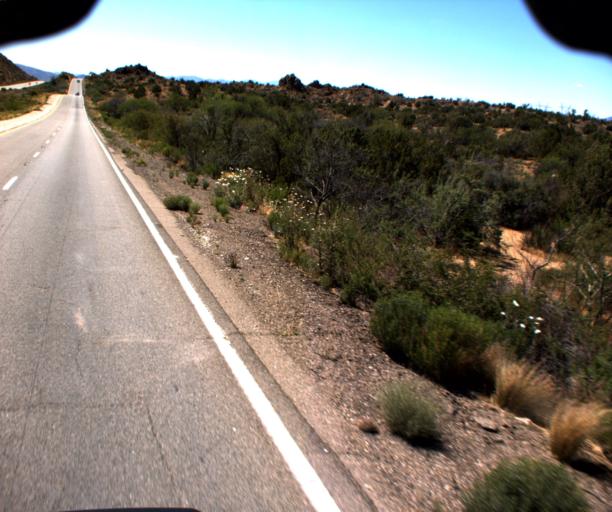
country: US
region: Arizona
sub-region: Yavapai County
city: Bagdad
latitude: 34.4799
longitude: -113.3383
